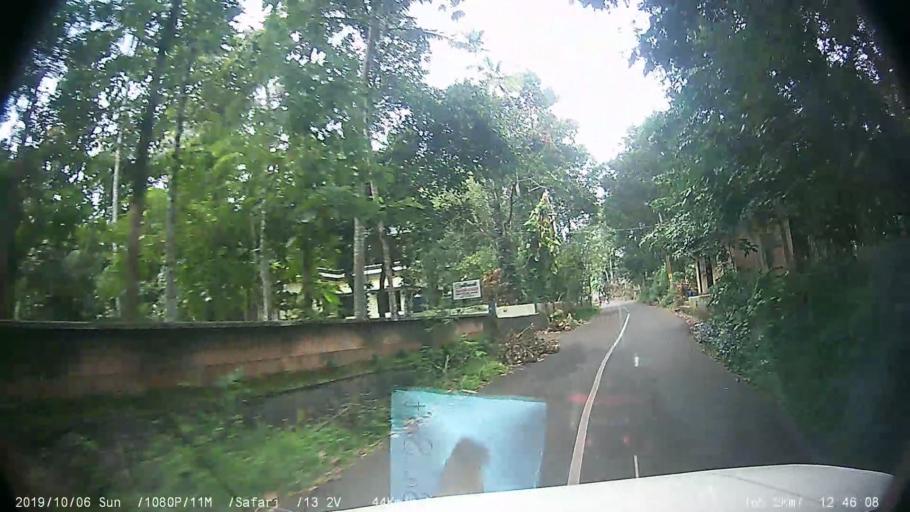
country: IN
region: Kerala
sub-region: Kottayam
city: Palackattumala
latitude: 9.7708
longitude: 76.6093
